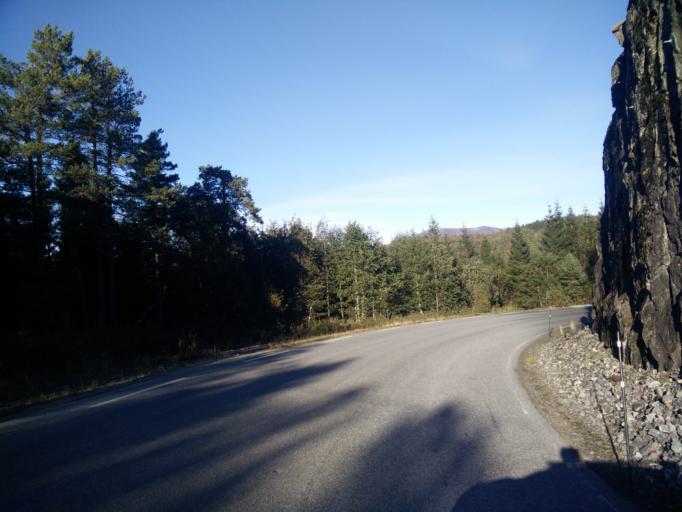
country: NO
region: More og Romsdal
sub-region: Halsa
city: Liaboen
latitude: 63.1033
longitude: 8.3350
